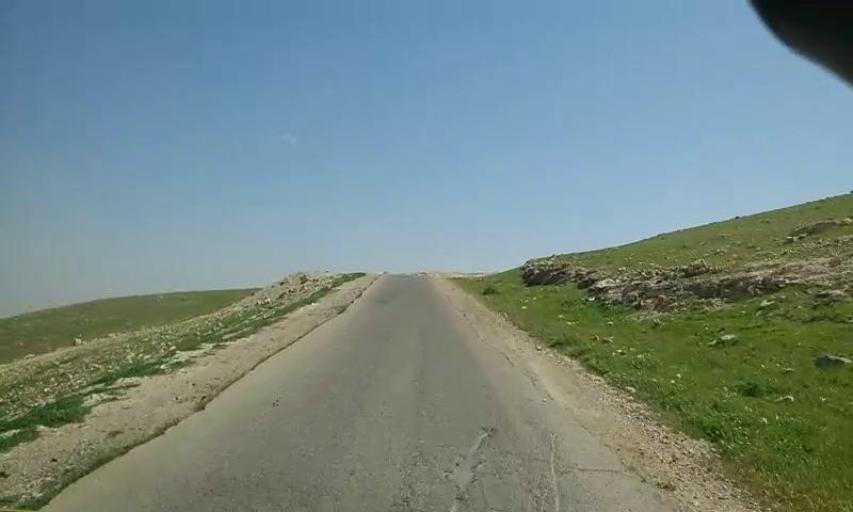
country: PS
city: `Arab ar Rashaydah
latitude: 31.5578
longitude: 35.2473
